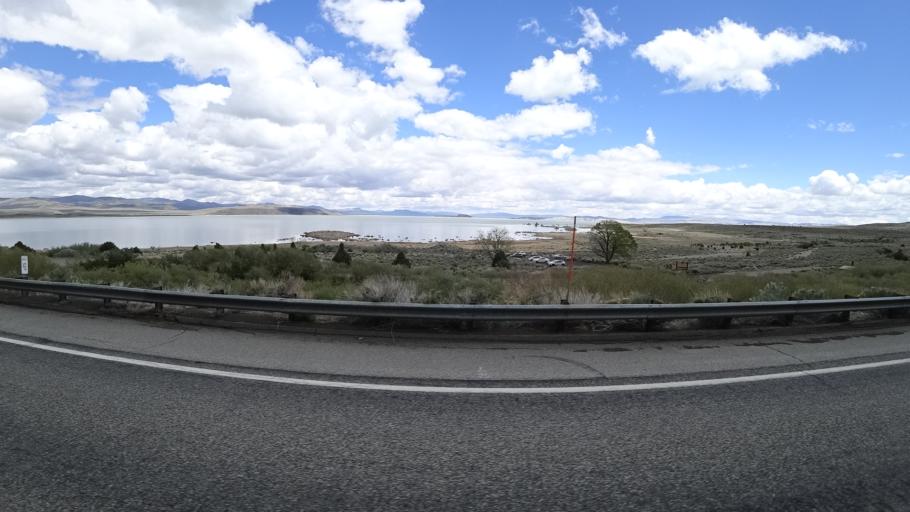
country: US
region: California
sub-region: Mono County
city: Bridgeport
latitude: 37.9765
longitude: -119.1355
